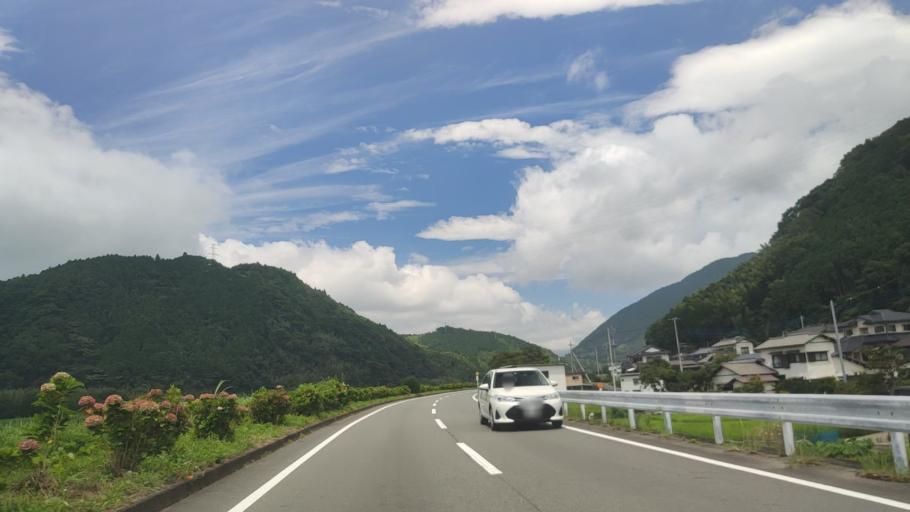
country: JP
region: Shizuoka
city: Fujinomiya
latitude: 35.2298
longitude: 138.5136
